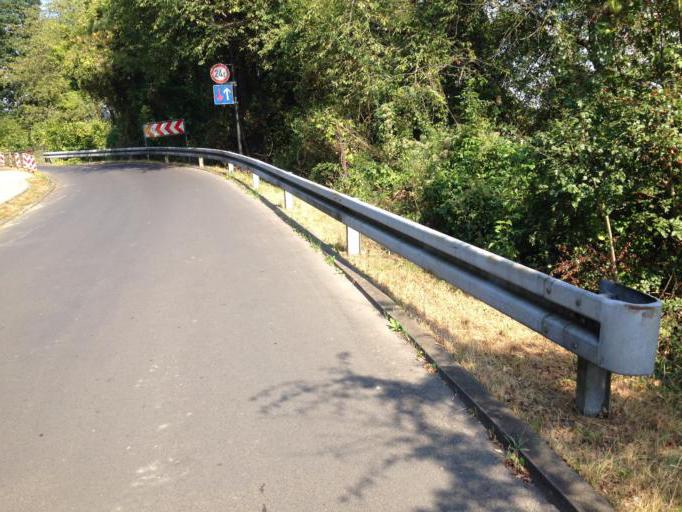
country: DE
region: Hesse
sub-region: Regierungsbezirk Giessen
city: Giessen
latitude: 50.6140
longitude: 8.6563
